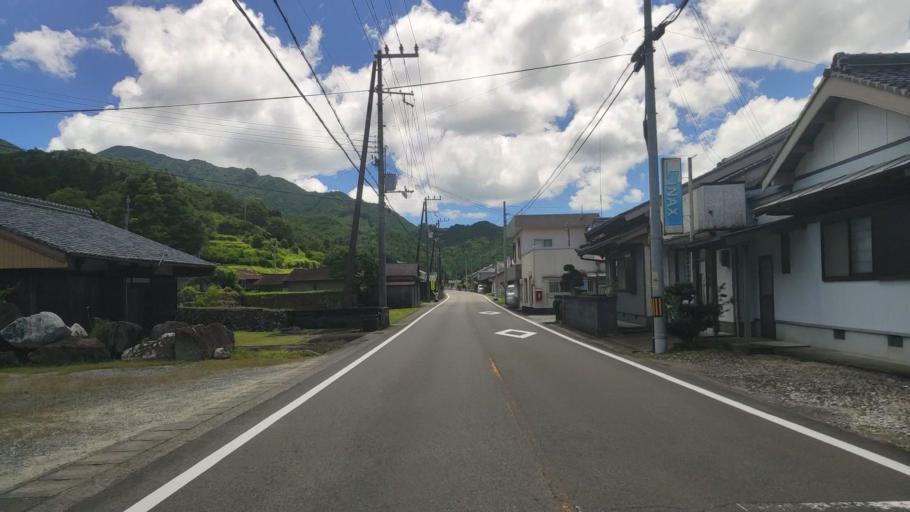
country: JP
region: Mie
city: Owase
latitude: 33.9769
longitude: 136.0539
